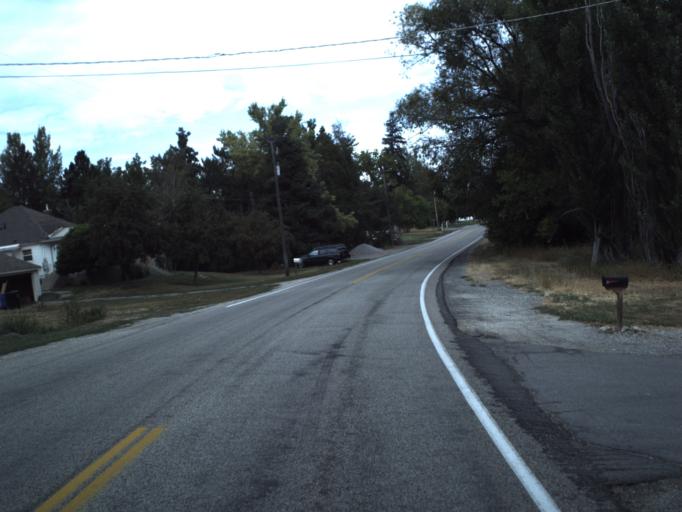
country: US
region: Utah
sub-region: Cache County
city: Mendon
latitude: 41.7041
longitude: -111.9793
